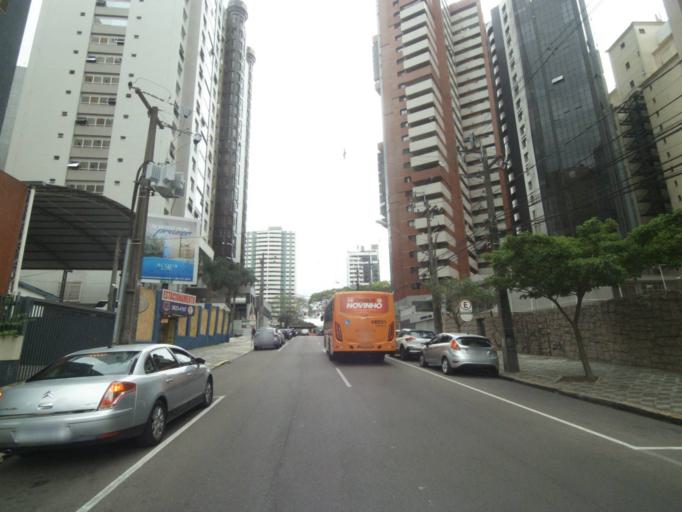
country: BR
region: Parana
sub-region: Curitiba
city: Curitiba
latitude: -25.4447
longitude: -49.2880
